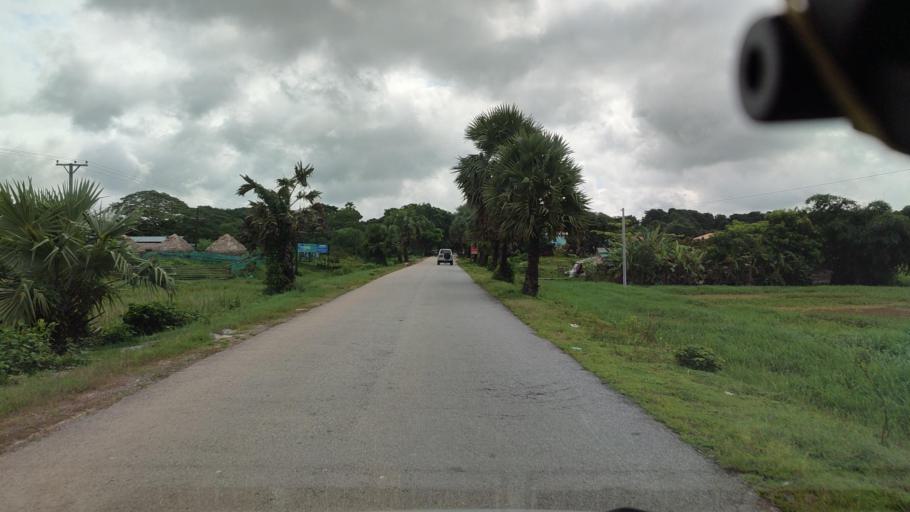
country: MM
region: Yangon
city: Kayan
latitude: 17.0997
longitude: 96.5050
